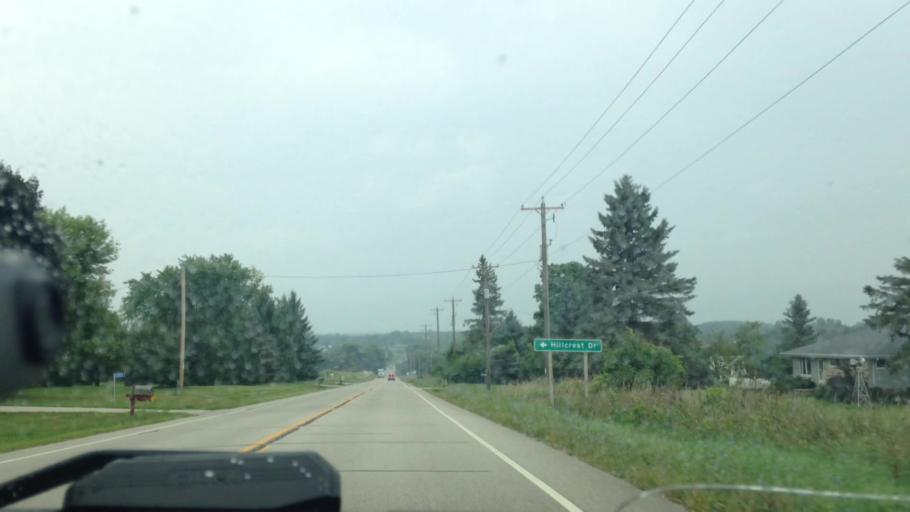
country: US
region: Wisconsin
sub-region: Washington County
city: Hartford
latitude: 43.4061
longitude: -88.3677
